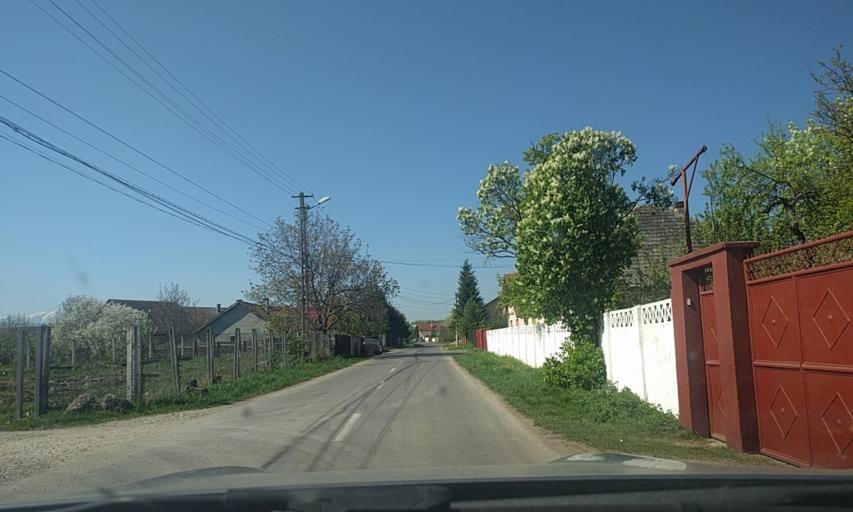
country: RO
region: Brasov
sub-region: Comuna Bod
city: Colonia Bod
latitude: 45.7118
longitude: 25.5783
